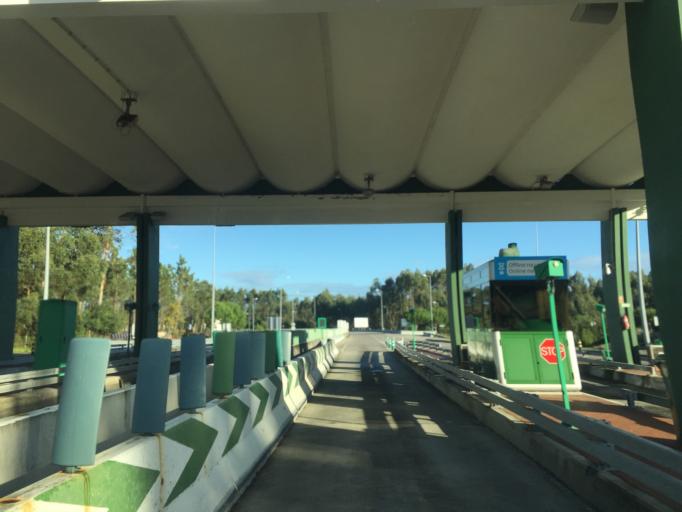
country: PT
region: Coimbra
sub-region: Figueira da Foz
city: Lavos
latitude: 40.0473
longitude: -8.8145
